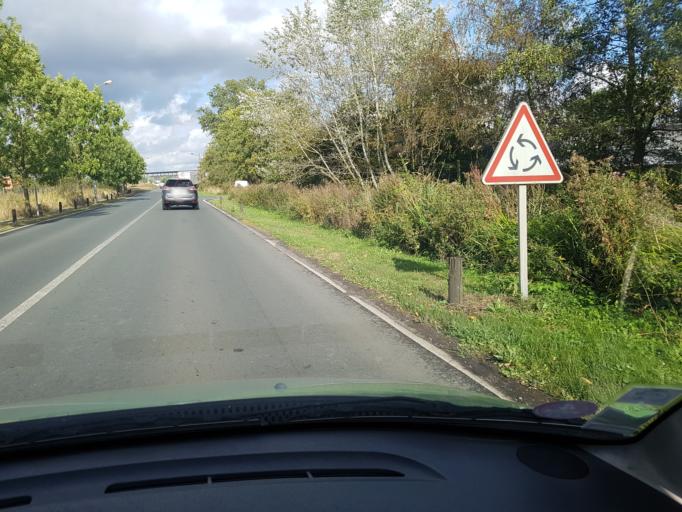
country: FR
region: Nord-Pas-de-Calais
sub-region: Departement du Nord
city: Bailleul
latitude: 50.7231
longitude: 2.7440
